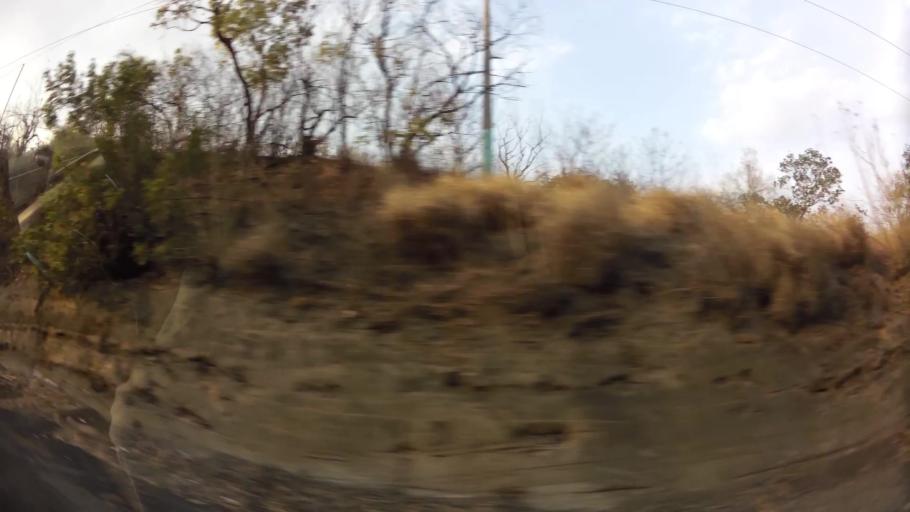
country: NI
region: Leon
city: Nagarote
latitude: 12.2689
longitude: -86.4771
